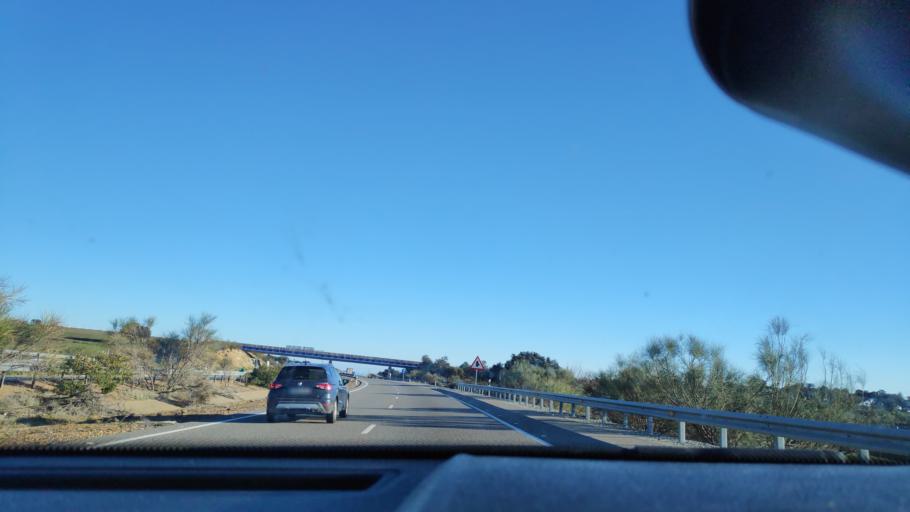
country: ES
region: Andalusia
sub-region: Provincia de Sevilla
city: Gerena
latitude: 37.6274
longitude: -6.1442
